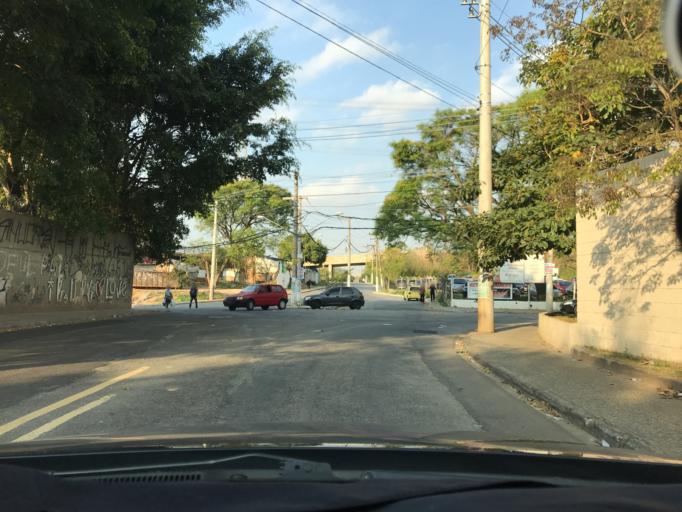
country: BR
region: Sao Paulo
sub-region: Osasco
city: Osasco
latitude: -23.5320
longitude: -46.7598
